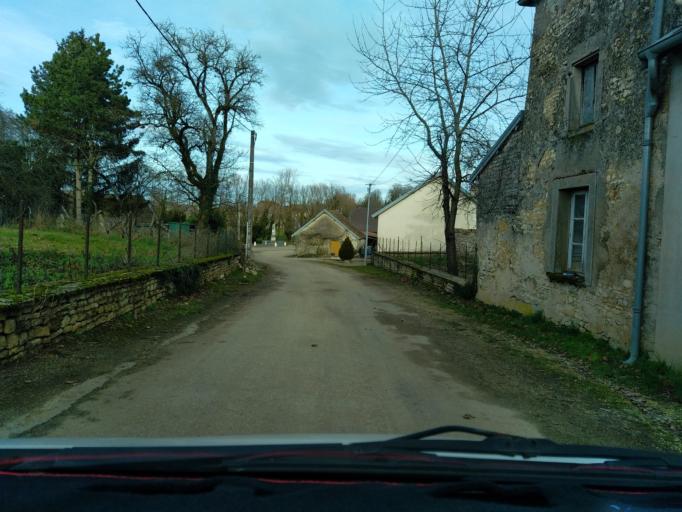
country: FR
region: Franche-Comte
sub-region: Departement de la Haute-Saone
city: Marnay
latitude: 47.3641
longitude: 5.7166
